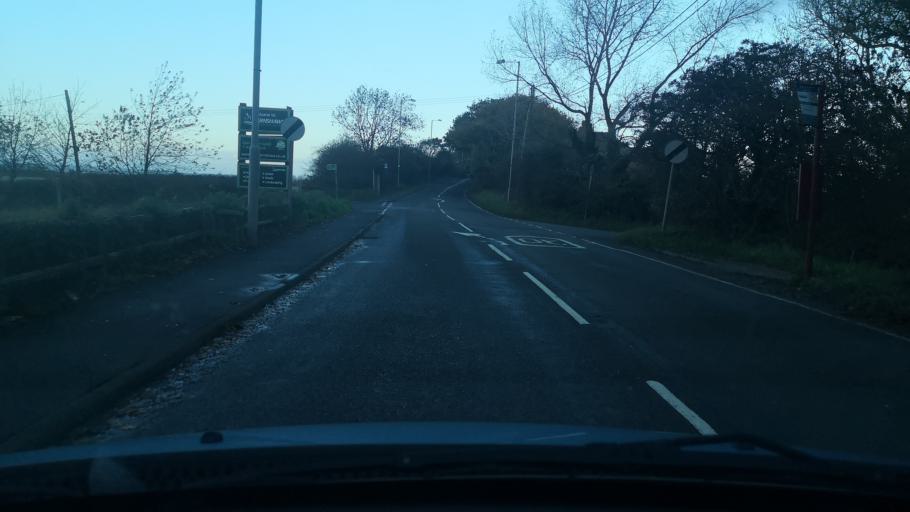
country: GB
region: England
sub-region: City and Borough of Wakefield
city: Middlestown
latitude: 53.6333
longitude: -1.5868
